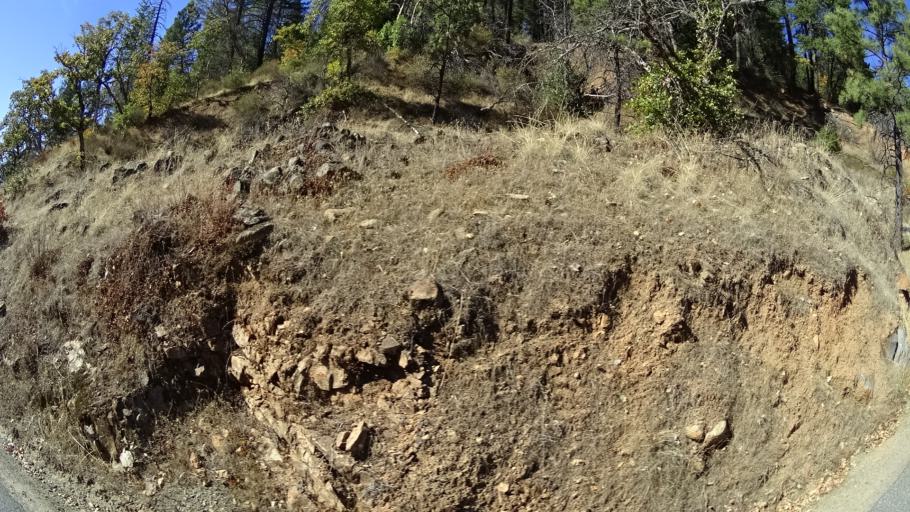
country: US
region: California
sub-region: Siskiyou County
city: Happy Camp
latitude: 41.3074
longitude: -123.2045
